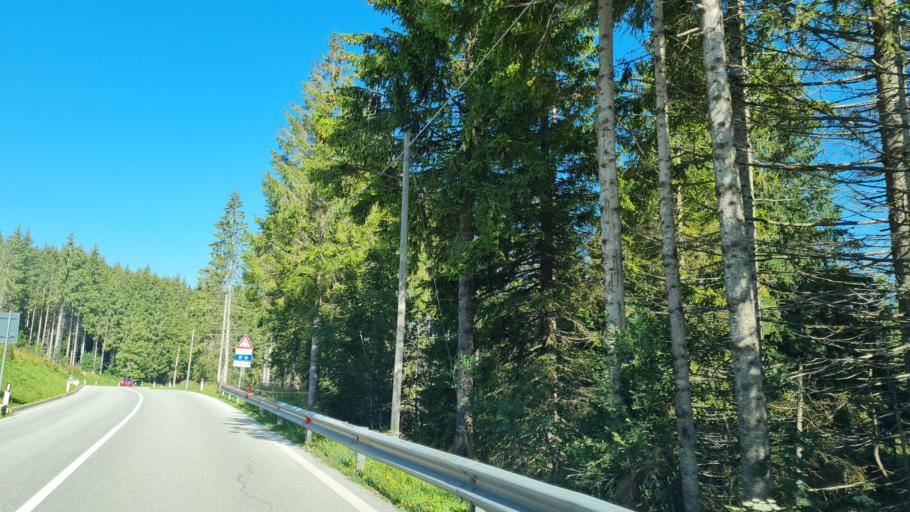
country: IT
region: Trentino-Alto Adige
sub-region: Provincia di Trento
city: Luserna
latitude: 45.9572
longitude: 11.3271
